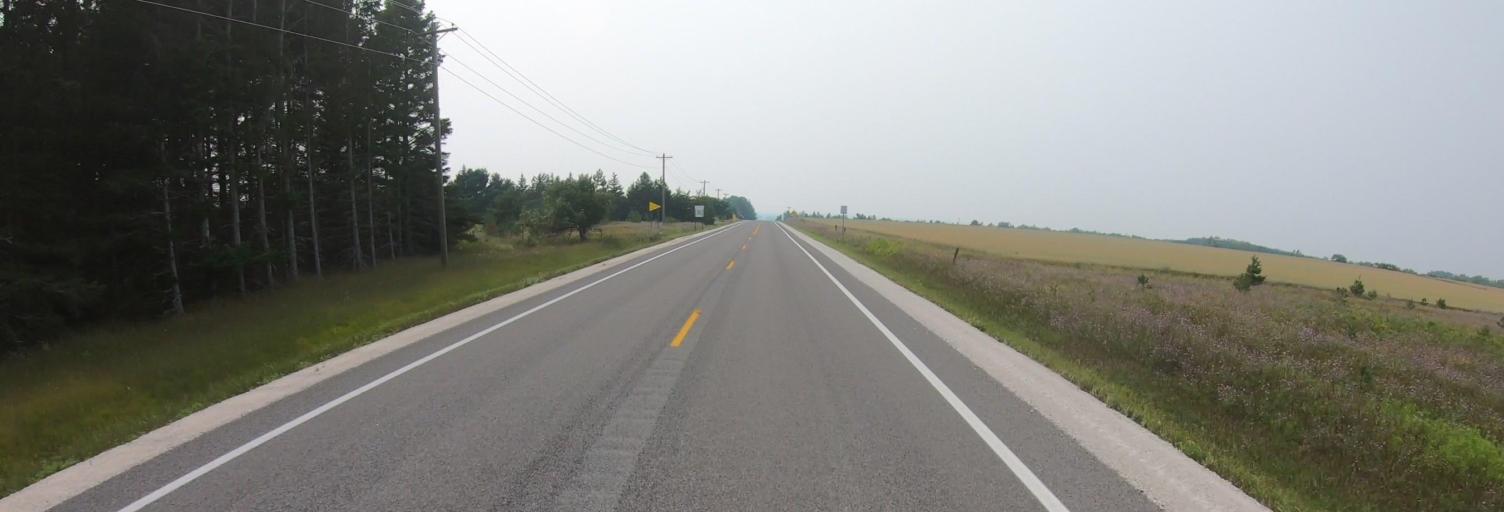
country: US
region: Michigan
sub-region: Chippewa County
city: Sault Ste. Marie
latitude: 46.0721
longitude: -84.1696
